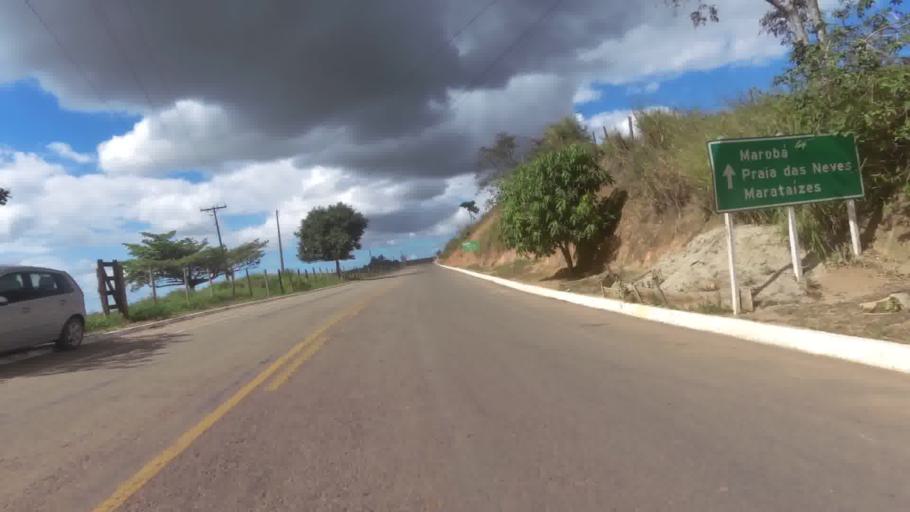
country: BR
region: Espirito Santo
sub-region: Marataizes
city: Marataizes
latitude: -21.1052
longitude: -41.0407
